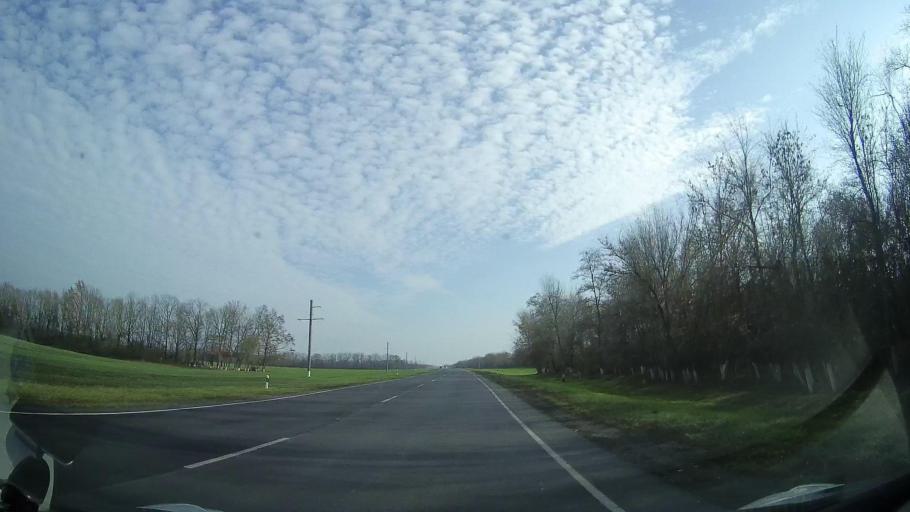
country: RU
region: Rostov
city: Gigant
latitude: 46.5287
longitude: 41.1974
